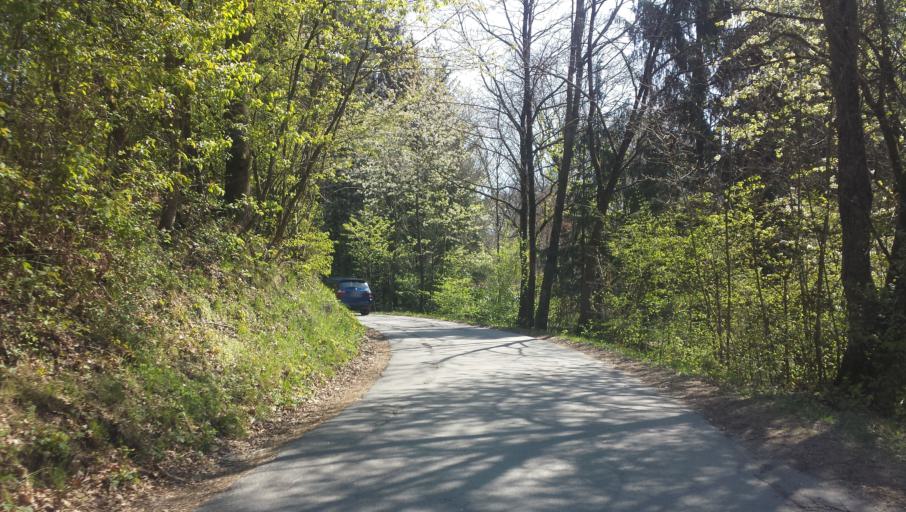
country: DE
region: Hesse
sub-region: Regierungsbezirk Darmstadt
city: Morlenbach
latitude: 49.6274
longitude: 8.7187
